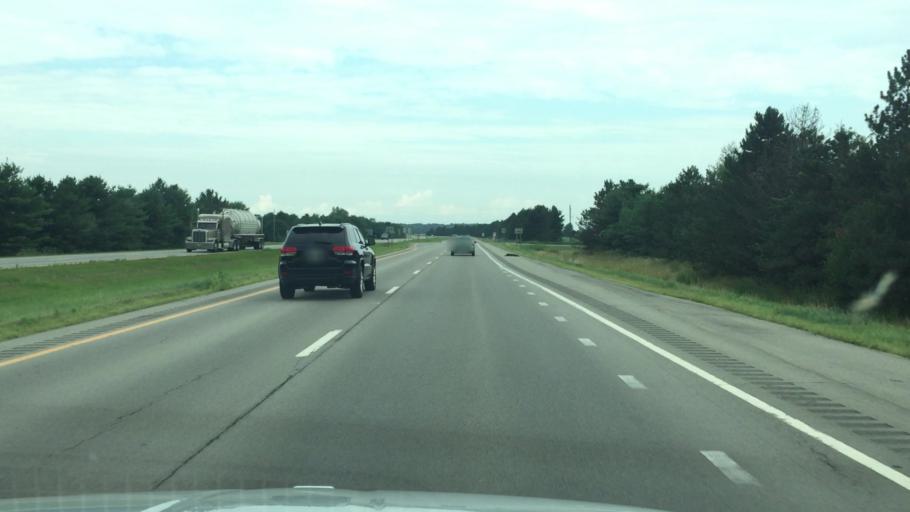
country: US
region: Ohio
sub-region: Wyandot County
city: Carey
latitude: 40.9743
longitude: -83.4893
